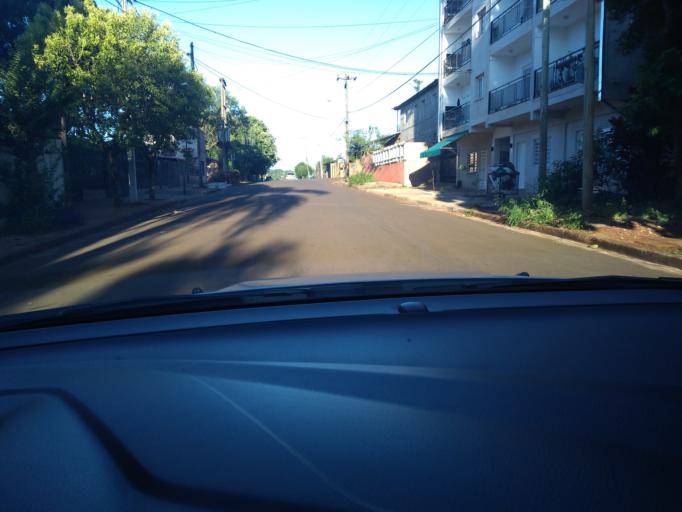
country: AR
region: Misiones
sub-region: Departamento de Obera
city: Obera
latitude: -27.4812
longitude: -55.1138
